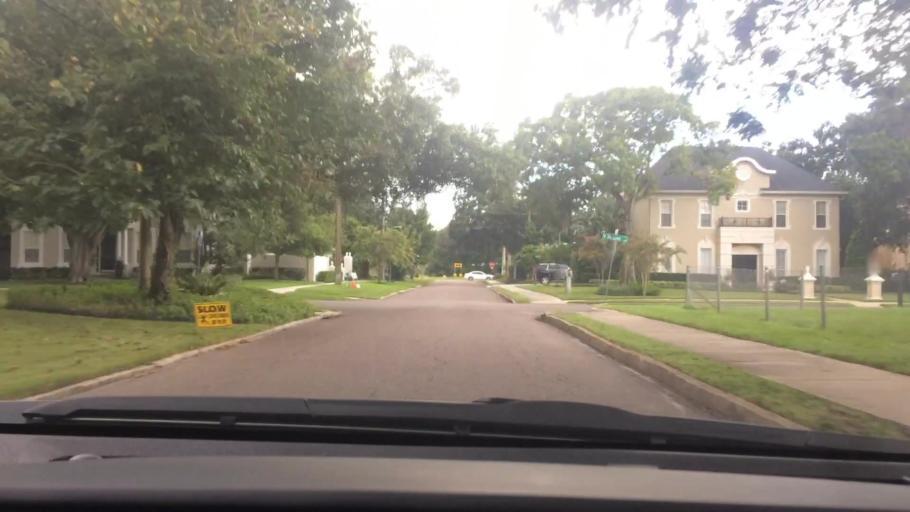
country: US
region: Florida
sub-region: Hillsborough County
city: Tampa
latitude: 27.9388
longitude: -82.5100
